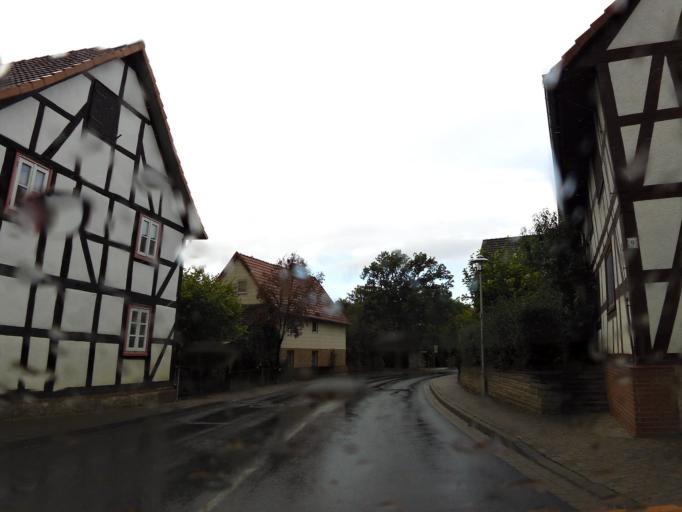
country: DE
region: Lower Saxony
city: Rosdorf
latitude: 51.4554
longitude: 9.8854
